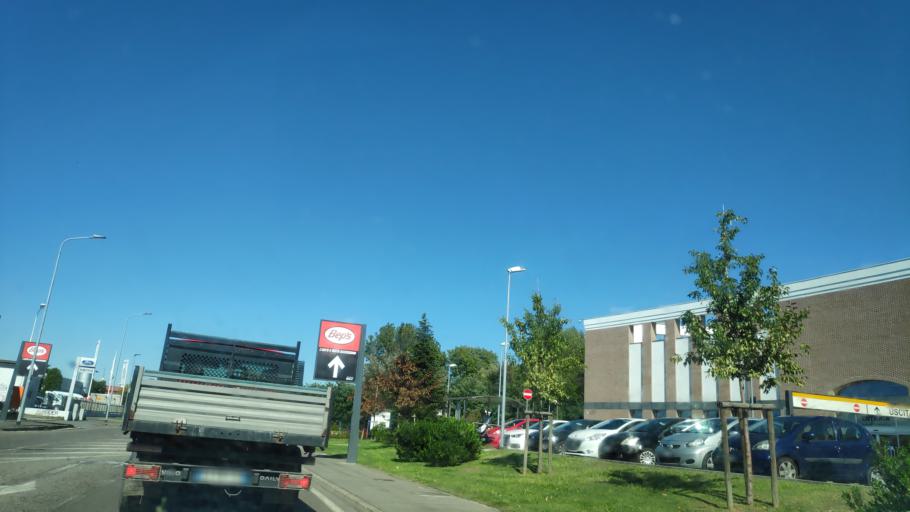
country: IT
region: Lombardy
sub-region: Citta metropolitana di Milano
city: Rozzano
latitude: 45.3779
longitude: 9.1695
